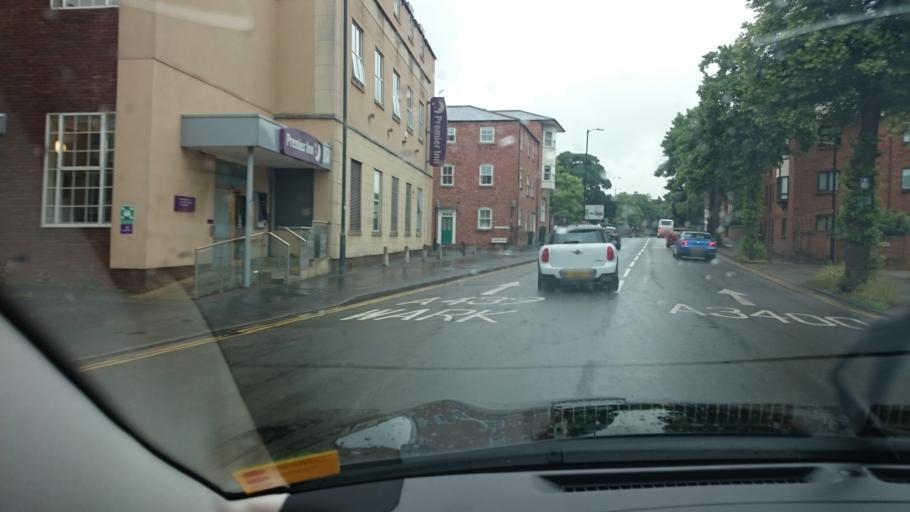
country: GB
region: England
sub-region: Warwickshire
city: Stratford-upon-Avon
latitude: 52.1937
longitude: -1.7038
